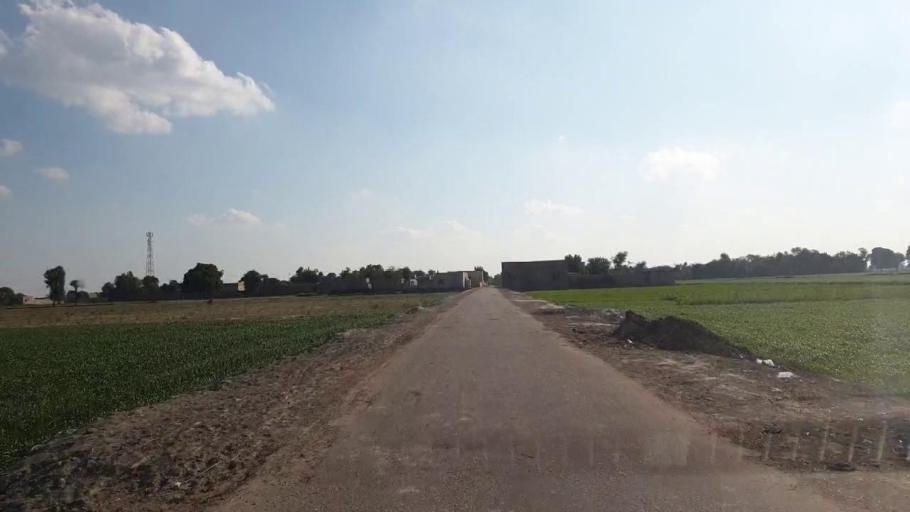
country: PK
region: Sindh
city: Shahpur Chakar
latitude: 26.1071
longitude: 68.5645
